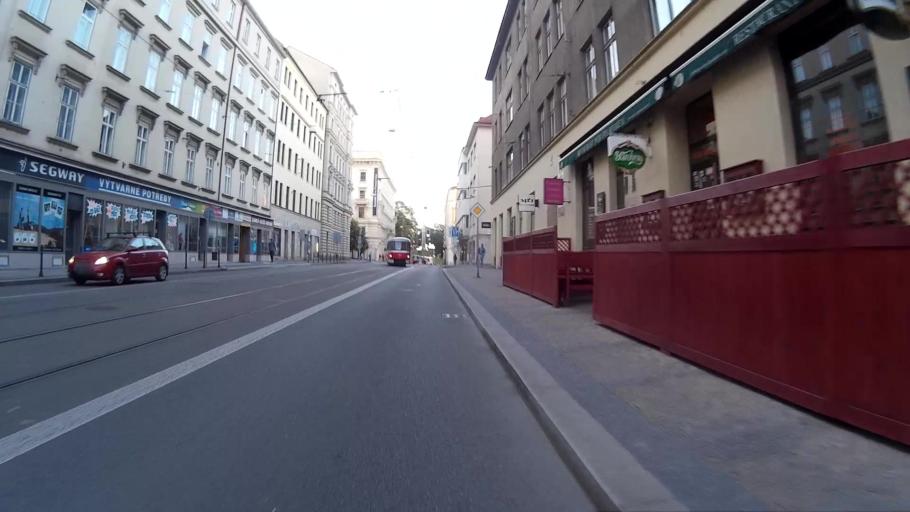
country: CZ
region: South Moravian
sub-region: Mesto Brno
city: Brno
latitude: 49.1930
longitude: 16.6047
